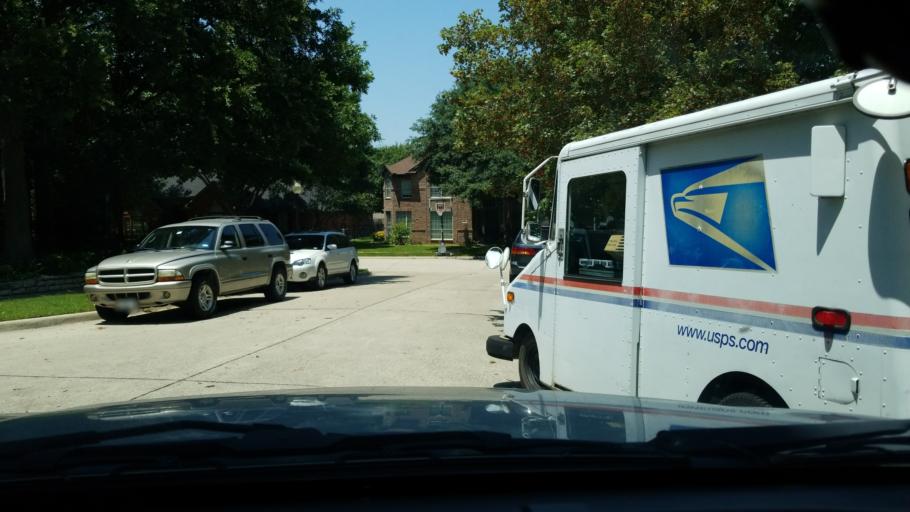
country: US
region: Texas
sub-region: Dallas County
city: Coppell
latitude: 32.9701
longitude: -96.9818
